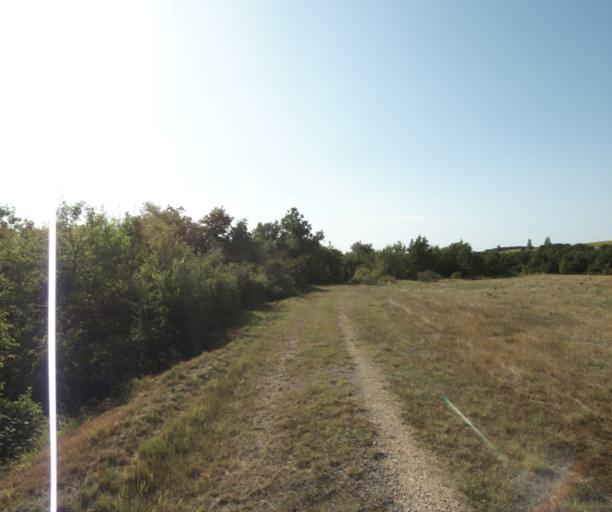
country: FR
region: Midi-Pyrenees
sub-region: Departement de la Haute-Garonne
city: Saint-Felix-Lauragais
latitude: 43.4443
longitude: 1.8212
